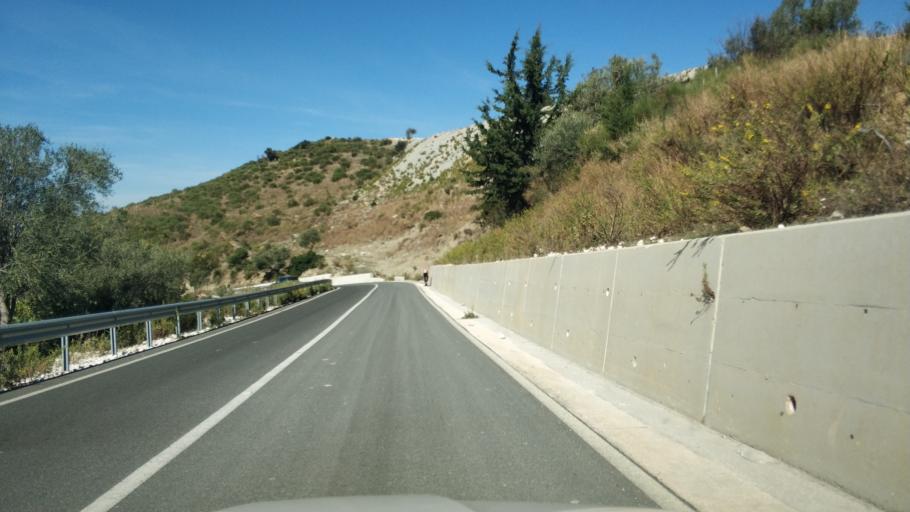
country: AL
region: Vlore
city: Vlore
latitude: 40.4559
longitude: 19.5141
